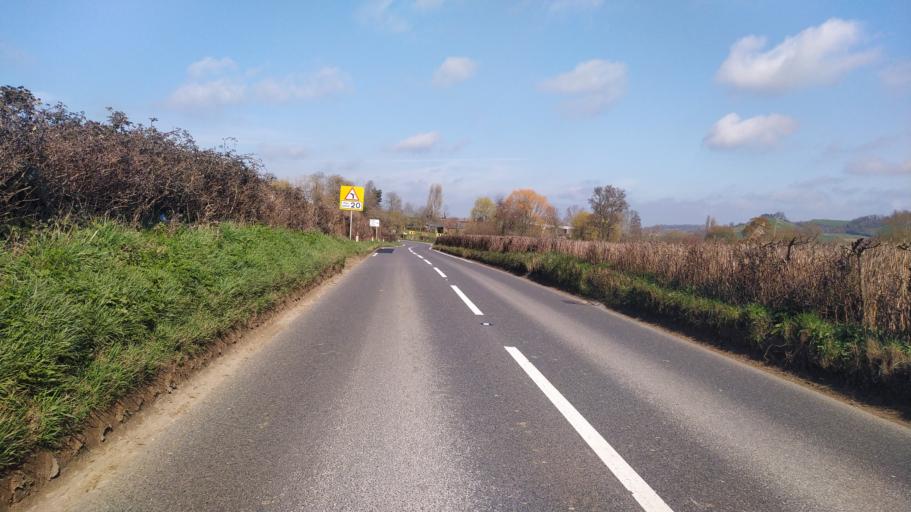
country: GB
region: England
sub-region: Somerset
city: Merriott
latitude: 50.9147
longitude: -2.7727
